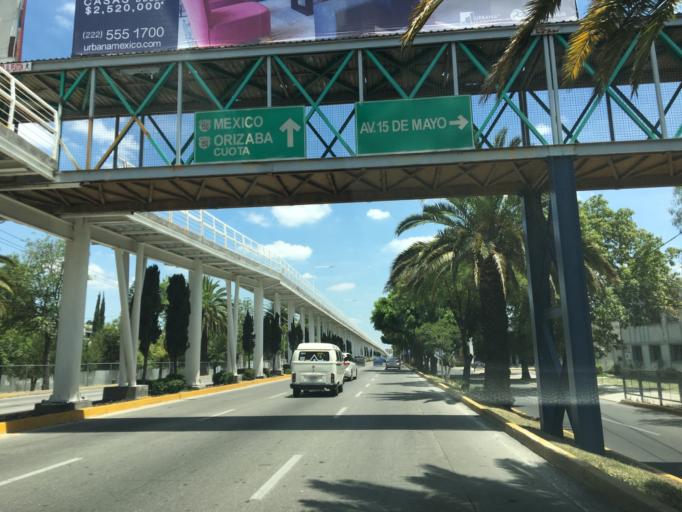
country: MX
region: Puebla
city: Puebla
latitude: 19.0645
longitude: -98.2225
